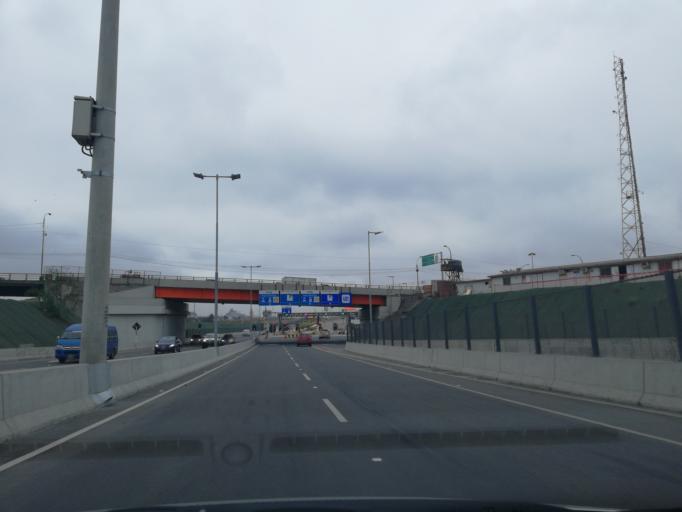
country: PE
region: Lima
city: Lima
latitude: -12.0435
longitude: -77.0186
